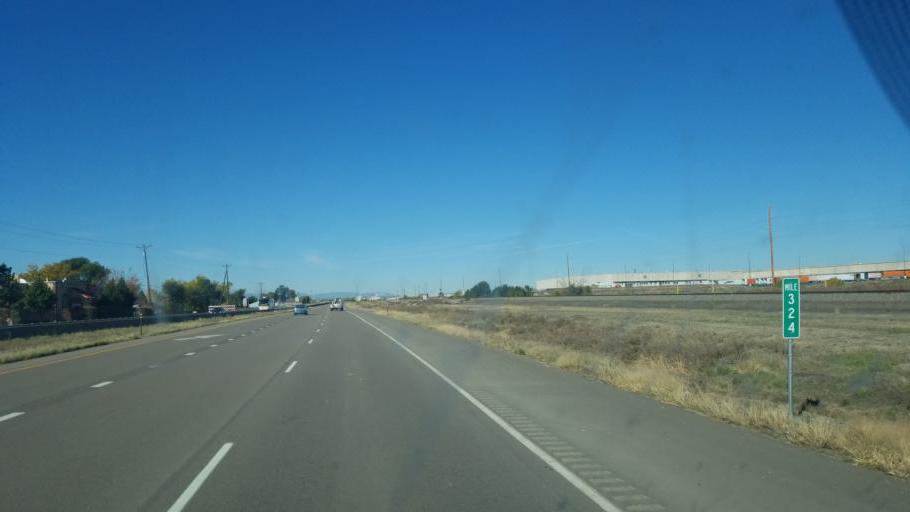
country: US
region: Colorado
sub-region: Pueblo County
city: Pueblo
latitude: 38.2752
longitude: -104.4615
